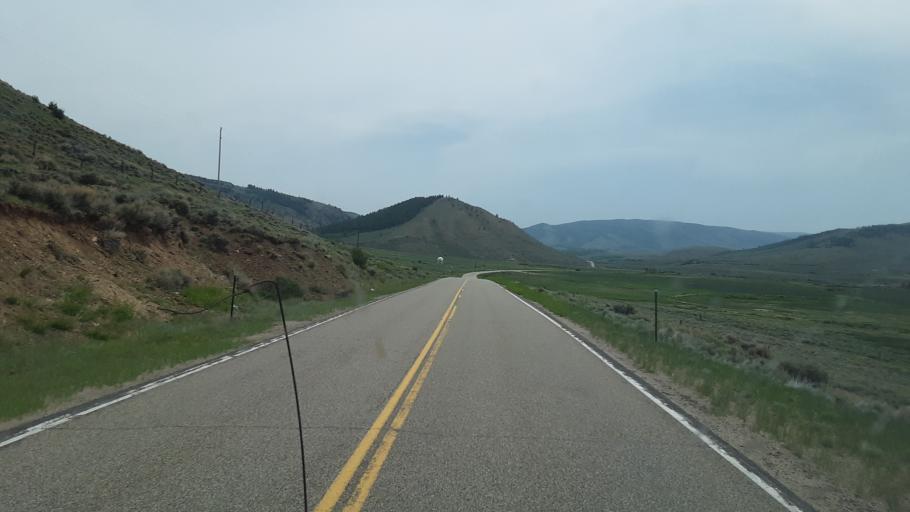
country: US
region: Colorado
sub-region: Jackson County
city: Walden
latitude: 40.9177
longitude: -106.3068
